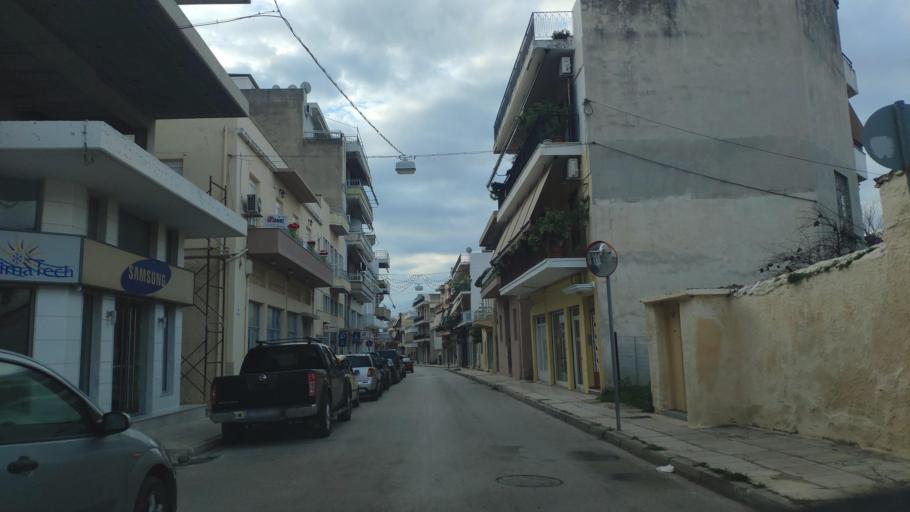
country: GR
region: Peloponnese
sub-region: Nomos Argolidos
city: Argos
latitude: 37.6400
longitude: 22.7291
